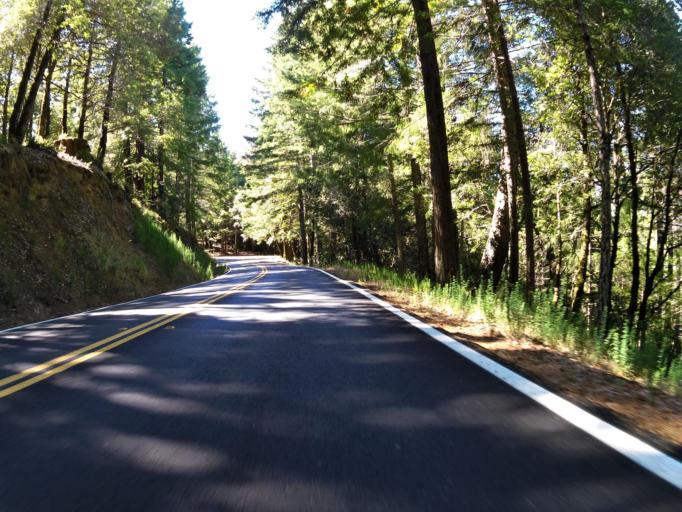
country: US
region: California
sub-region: Humboldt County
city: Redway
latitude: 39.8348
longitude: -123.7744
